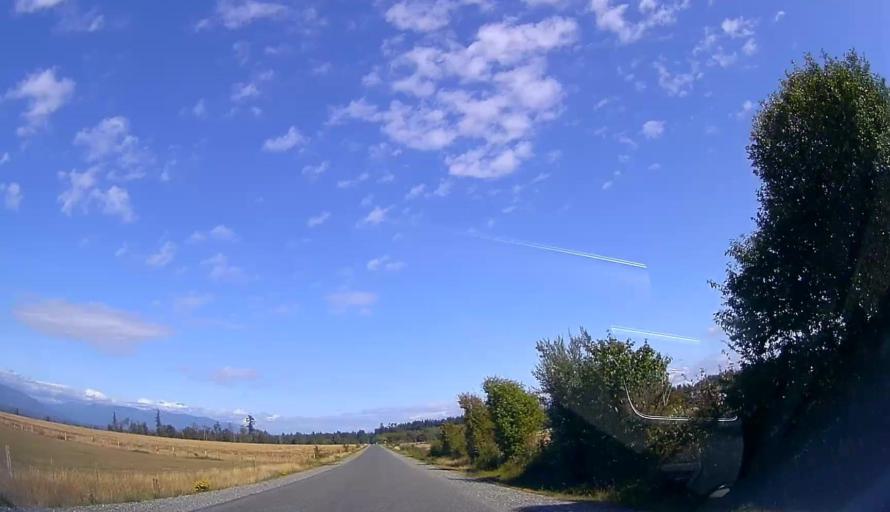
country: US
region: Washington
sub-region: Skagit County
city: Burlington
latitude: 48.5011
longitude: -122.4675
